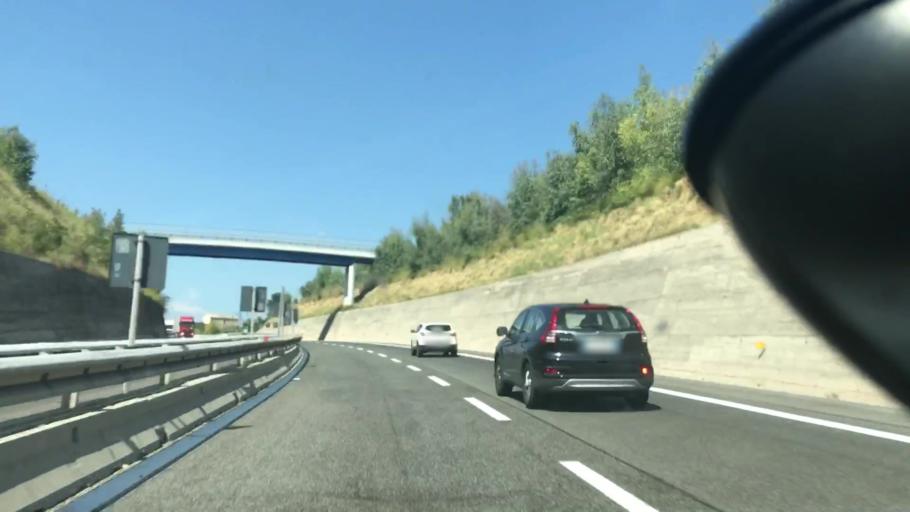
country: IT
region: Abruzzo
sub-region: Provincia di Chieti
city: San Vito Chietino
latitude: 42.2983
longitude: 14.4312
